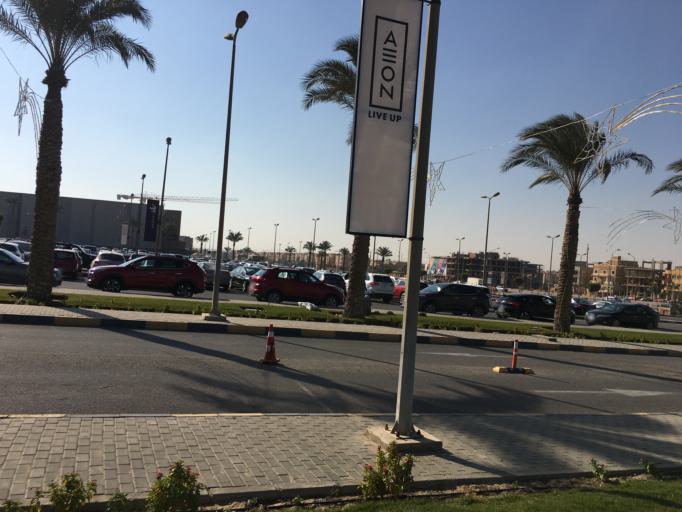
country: EG
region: Al Jizah
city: Awsim
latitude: 30.0080
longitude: 30.9732
